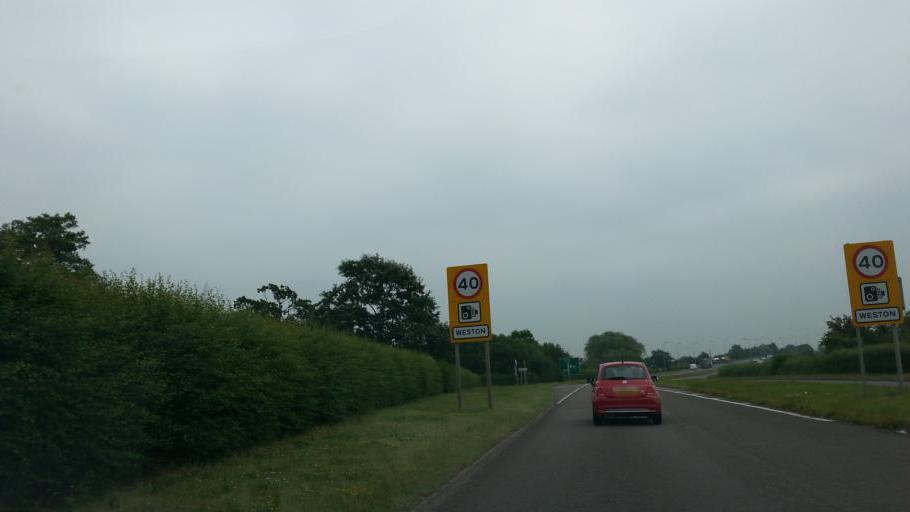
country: GB
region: England
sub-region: Staffordshire
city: Colwich
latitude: 52.8467
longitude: -2.0406
